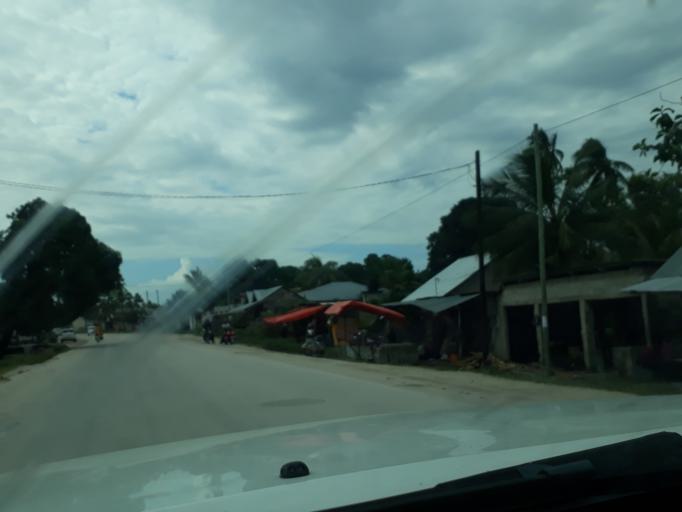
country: TZ
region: Zanzibar Central/South
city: Koani
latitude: -6.0849
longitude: 39.2227
